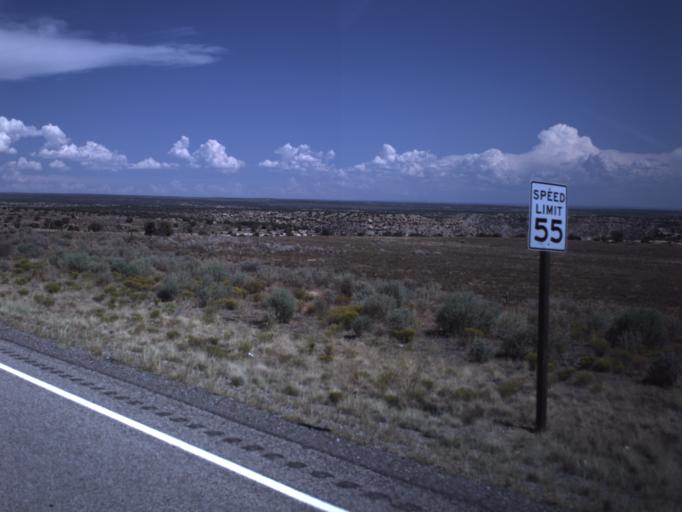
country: US
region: Utah
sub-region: San Juan County
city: Blanding
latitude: 37.4393
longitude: -109.4697
